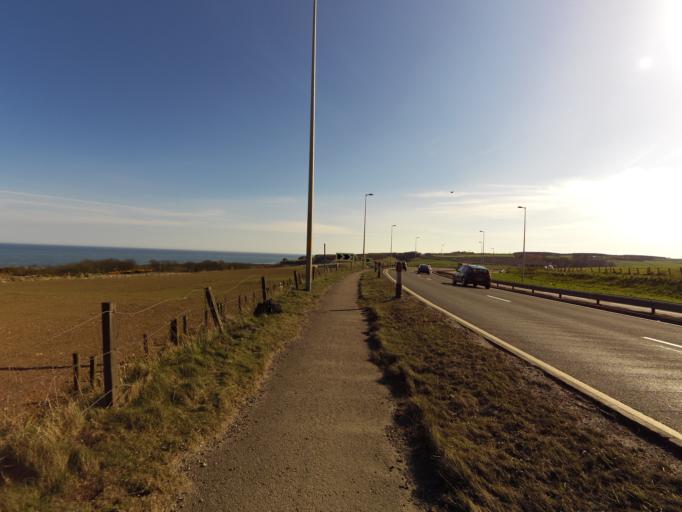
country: GB
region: Scotland
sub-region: Aberdeenshire
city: Newtonhill
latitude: 57.0154
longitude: -2.1681
